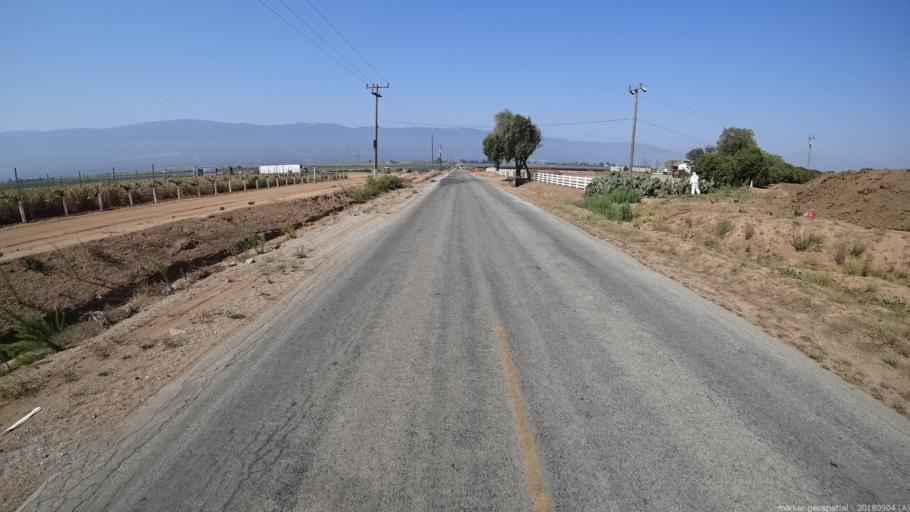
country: US
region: California
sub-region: Monterey County
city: Gonzales
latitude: 36.4977
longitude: -121.4125
